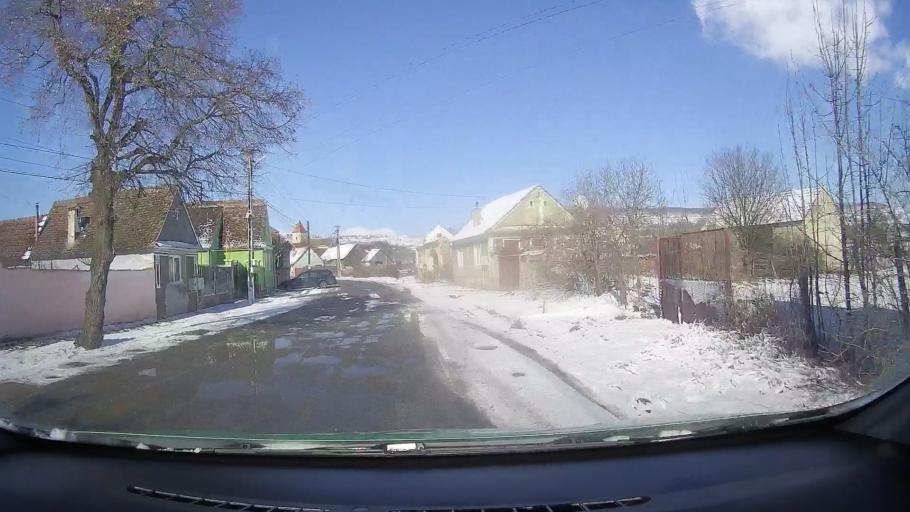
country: RO
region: Sibiu
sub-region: Comuna Avrig
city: Avrig
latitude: 45.7571
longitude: 24.3916
